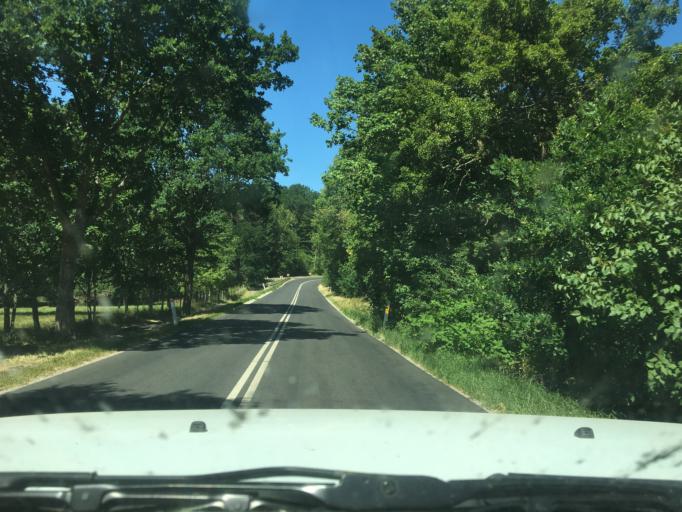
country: DK
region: Central Jutland
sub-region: Favrskov Kommune
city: Ulstrup
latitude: 56.3995
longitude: 9.7933
